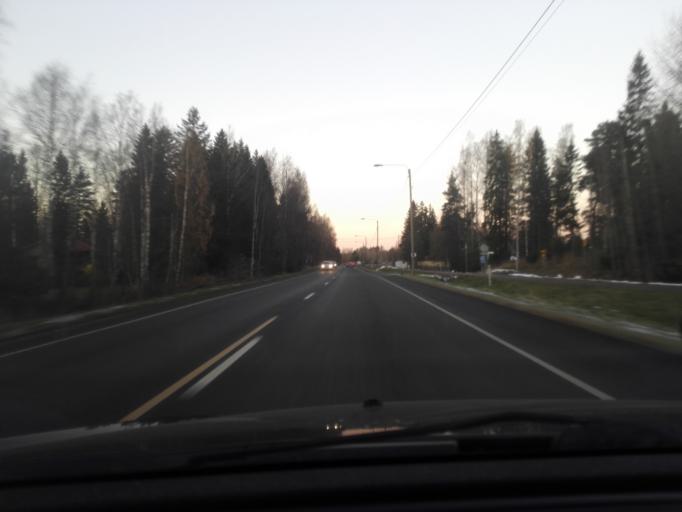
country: FI
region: Uusimaa
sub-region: Helsinki
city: Kerava
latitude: 60.3346
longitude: 25.1247
